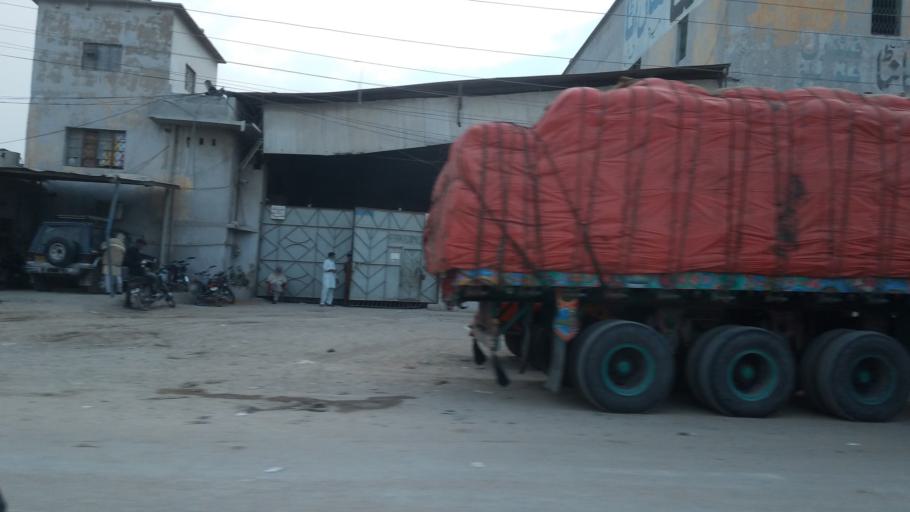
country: PK
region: Sindh
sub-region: Karachi District
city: Karachi
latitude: 24.9405
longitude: 67.0850
